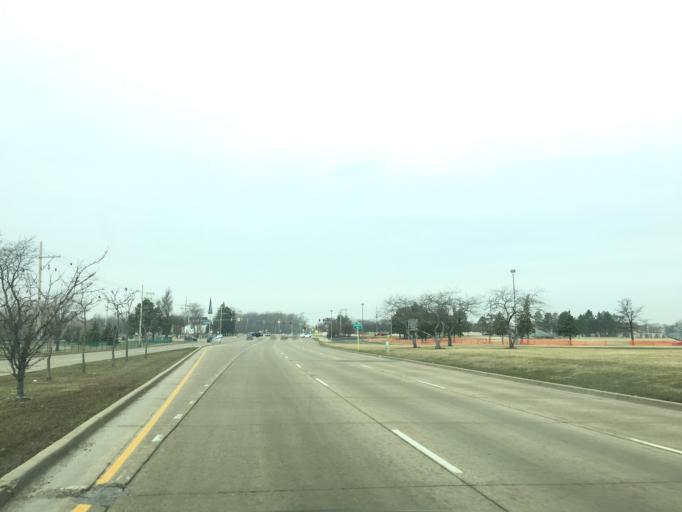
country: US
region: Illinois
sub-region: Cook County
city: Hoffman Estates
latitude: 42.0780
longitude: -88.0752
